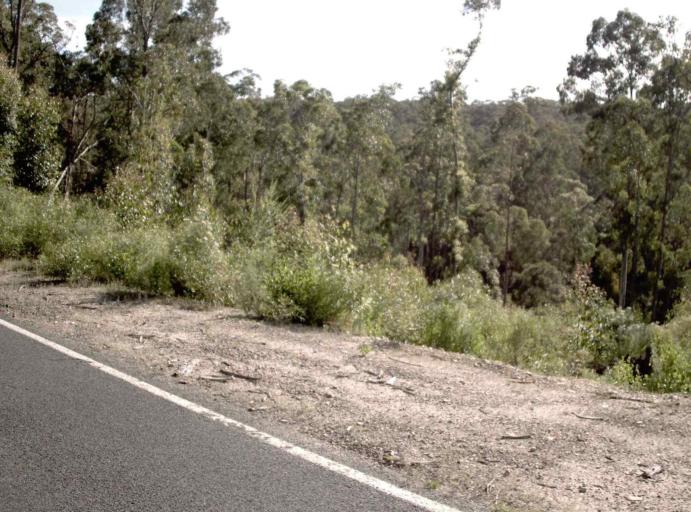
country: AU
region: Victoria
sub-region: East Gippsland
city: Lakes Entrance
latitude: -37.6669
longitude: 148.4779
